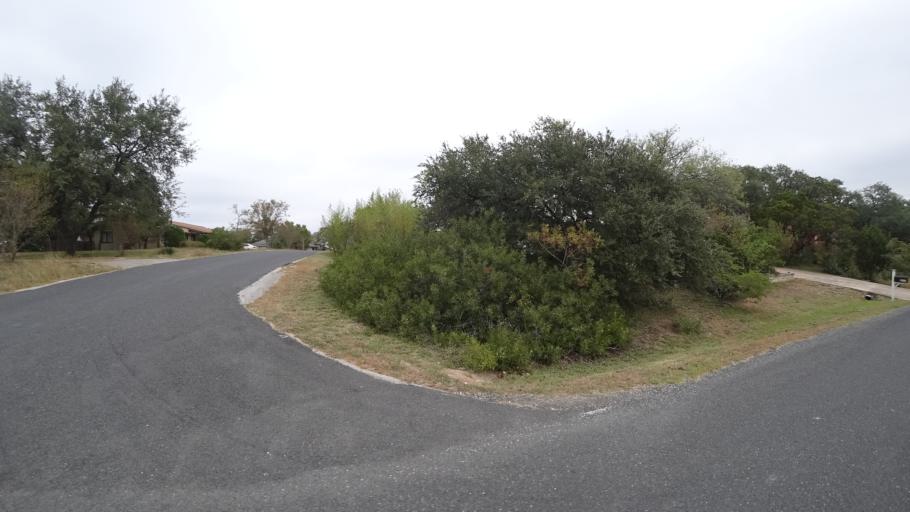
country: US
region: Texas
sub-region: Travis County
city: Barton Creek
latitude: 30.2416
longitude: -97.8885
